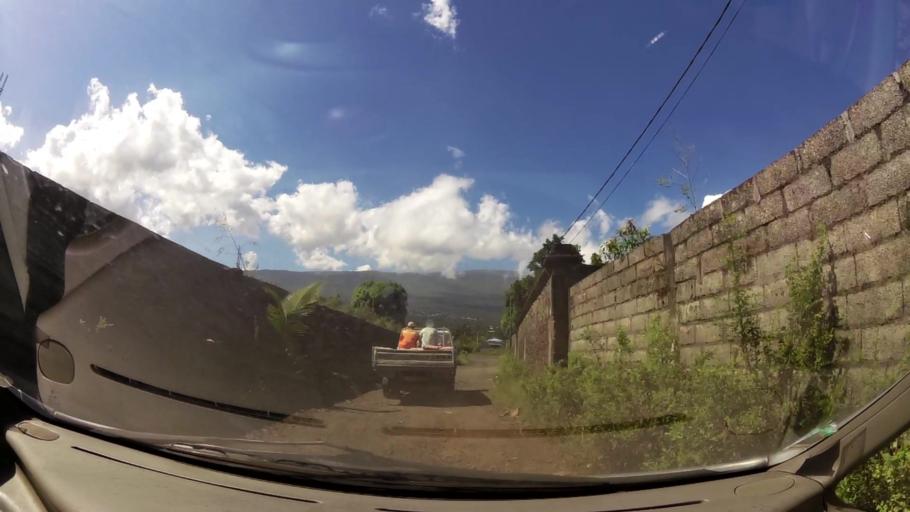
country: KM
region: Grande Comore
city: Mavingouni
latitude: -11.7299
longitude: 43.2416
